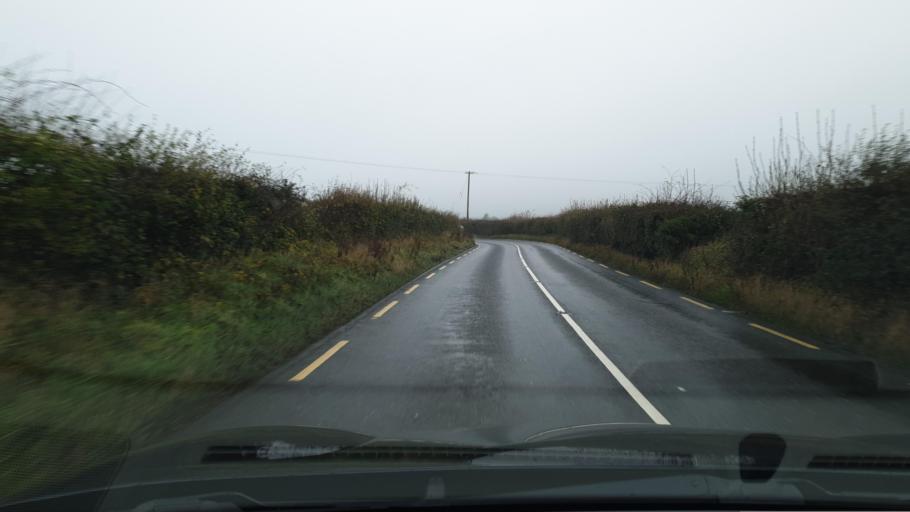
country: IE
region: Leinster
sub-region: An Mhi
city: Ashbourne
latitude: 53.4933
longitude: -6.3616
